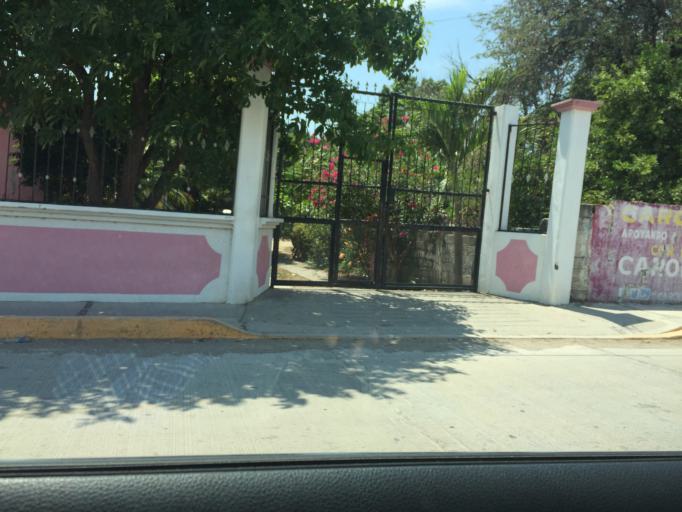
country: MX
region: Oaxaca
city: Asuncion Ixtaltepec
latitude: 16.5022
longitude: -95.0514
